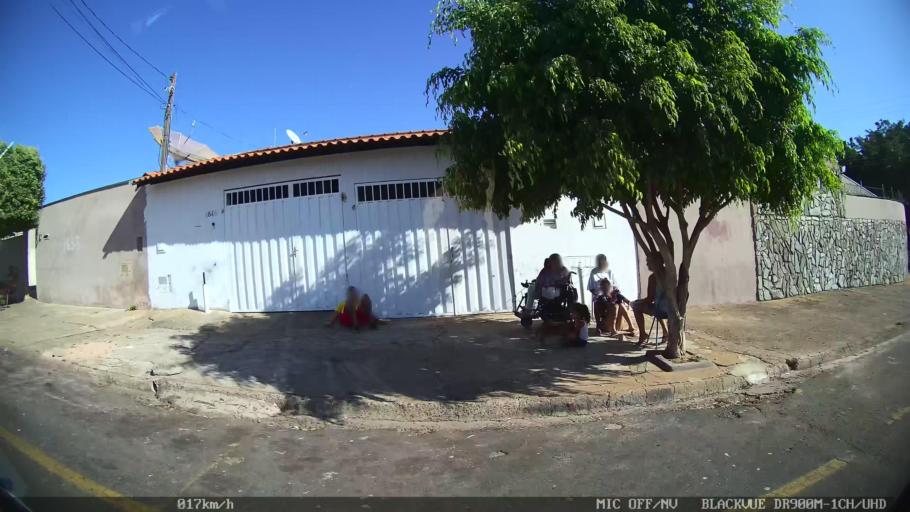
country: BR
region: Sao Paulo
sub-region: Franca
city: Franca
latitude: -20.4940
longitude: -47.4210
